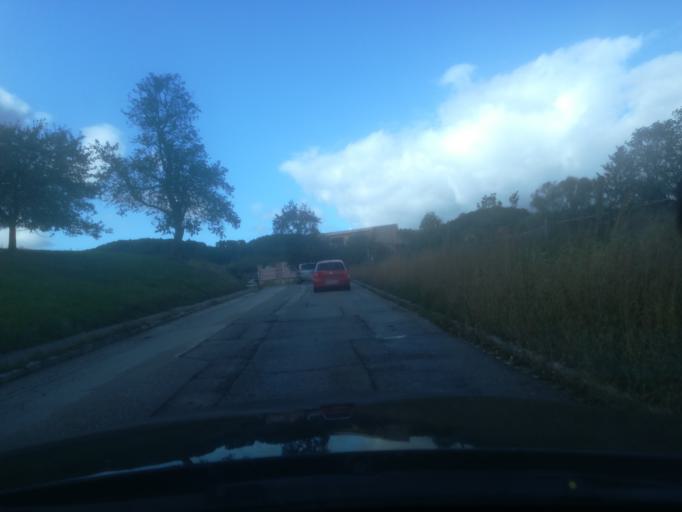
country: AT
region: Upper Austria
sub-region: Linz Stadt
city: Linz
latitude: 48.3358
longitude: 14.2773
